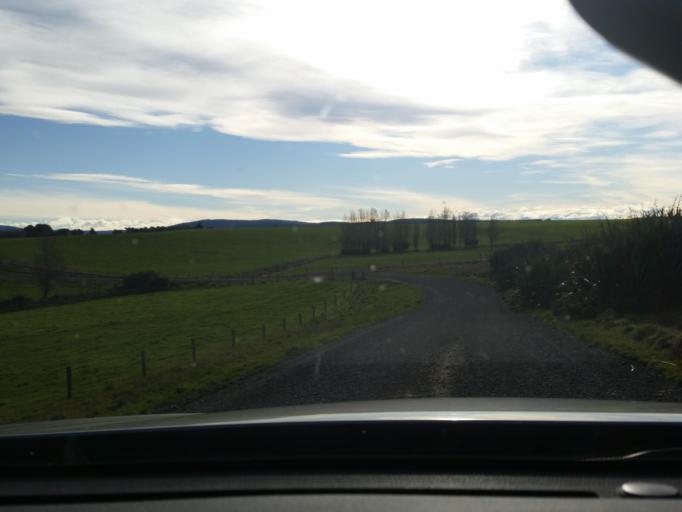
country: NZ
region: Southland
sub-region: Southland District
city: Riverton
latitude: -46.2752
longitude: 168.0405
